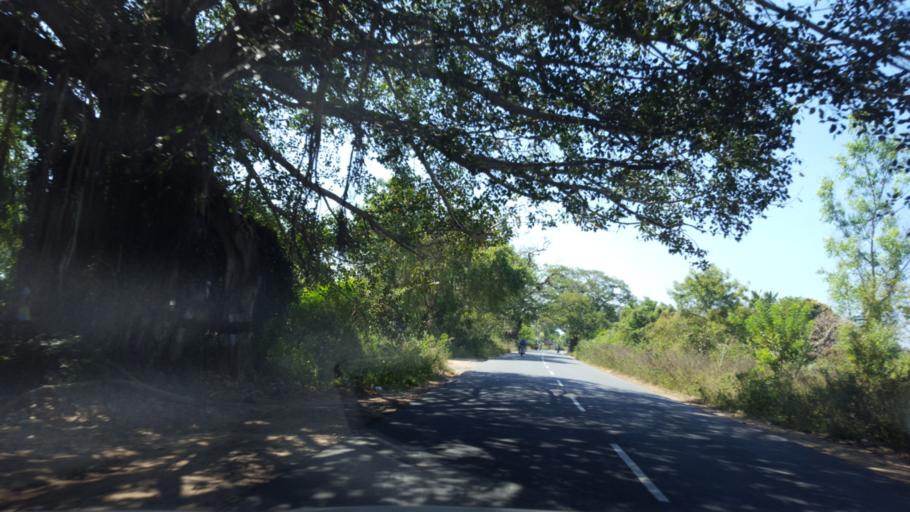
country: IN
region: Tamil Nadu
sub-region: Kancheepuram
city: Chengalpattu
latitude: 12.7532
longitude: 79.9303
